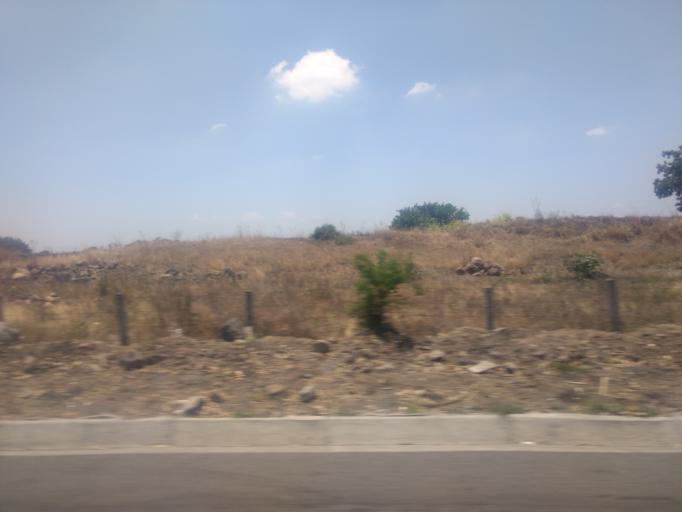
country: MX
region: Colima
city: Queseria
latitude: 19.3516
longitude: -103.5662
